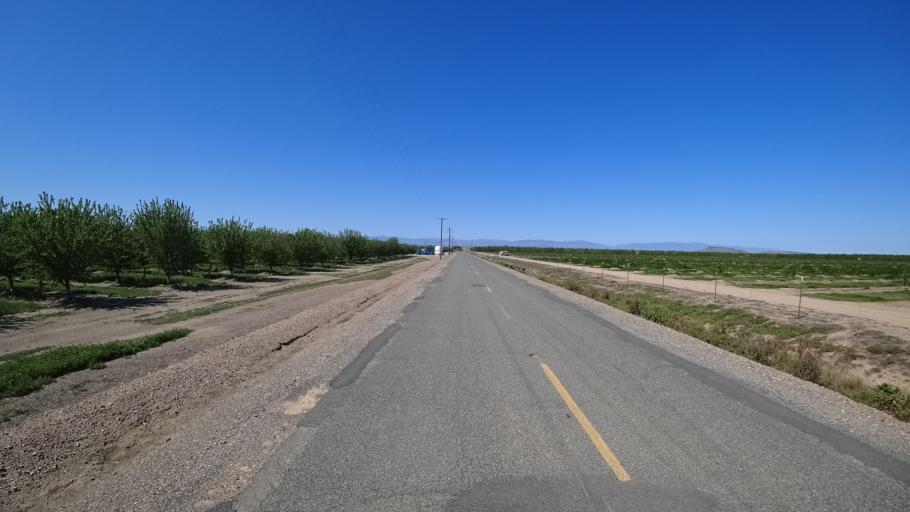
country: US
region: California
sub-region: Glenn County
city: Orland
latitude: 39.6972
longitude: -122.2442
